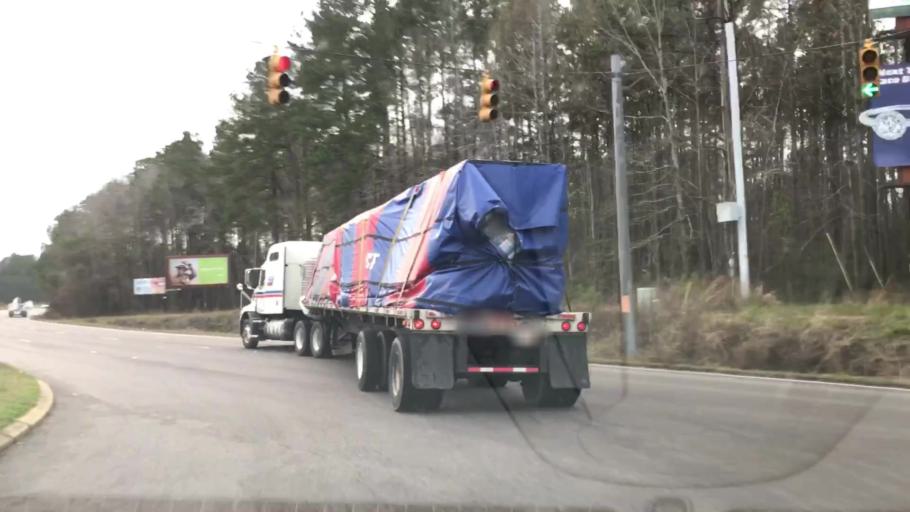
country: US
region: South Carolina
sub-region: Berkeley County
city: Moncks Corner
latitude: 33.2218
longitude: -79.9663
